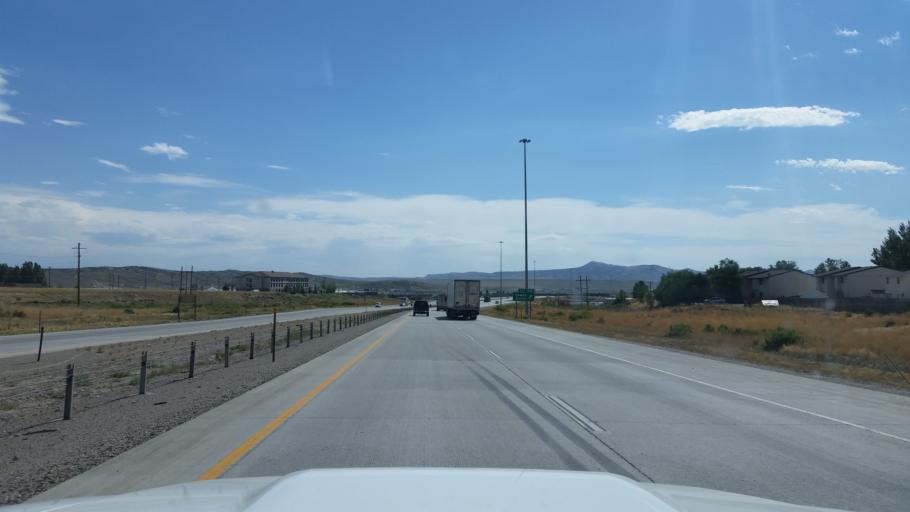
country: US
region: Wyoming
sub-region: Sweetwater County
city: Rock Springs
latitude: 41.5864
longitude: -109.2494
